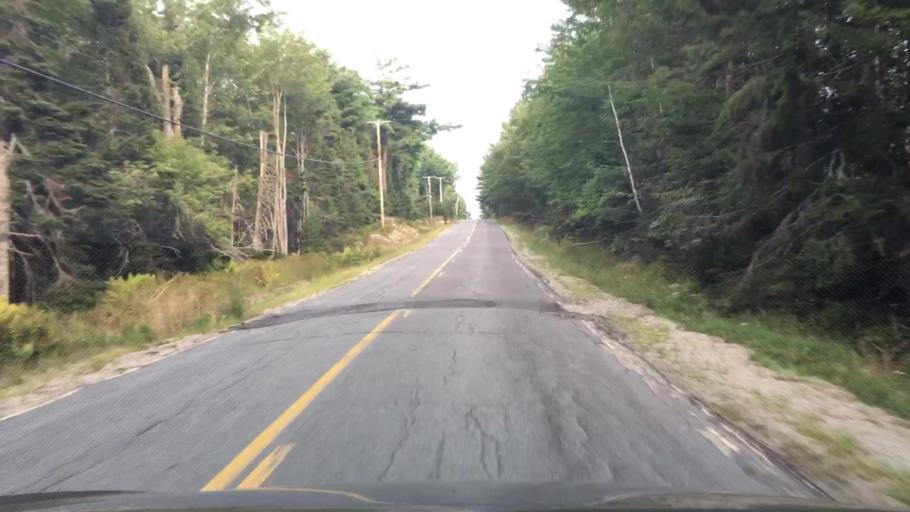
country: US
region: Maine
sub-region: Hancock County
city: Surry
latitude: 44.5001
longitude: -68.5609
